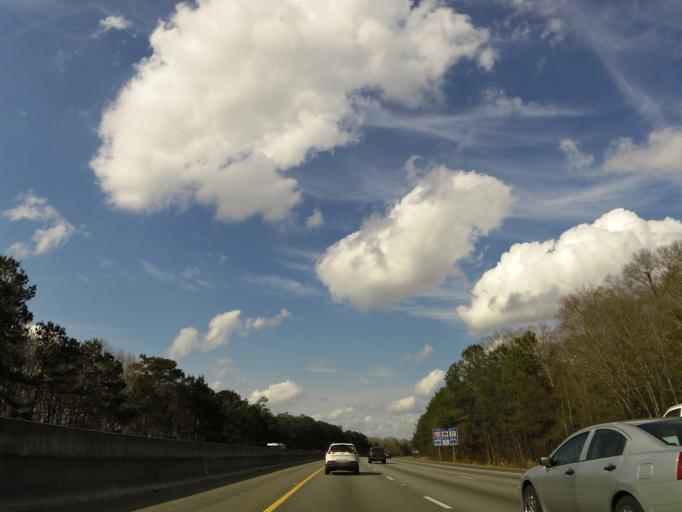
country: US
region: South Carolina
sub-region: Berkeley County
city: Ladson
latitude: 32.9629
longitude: -80.0731
